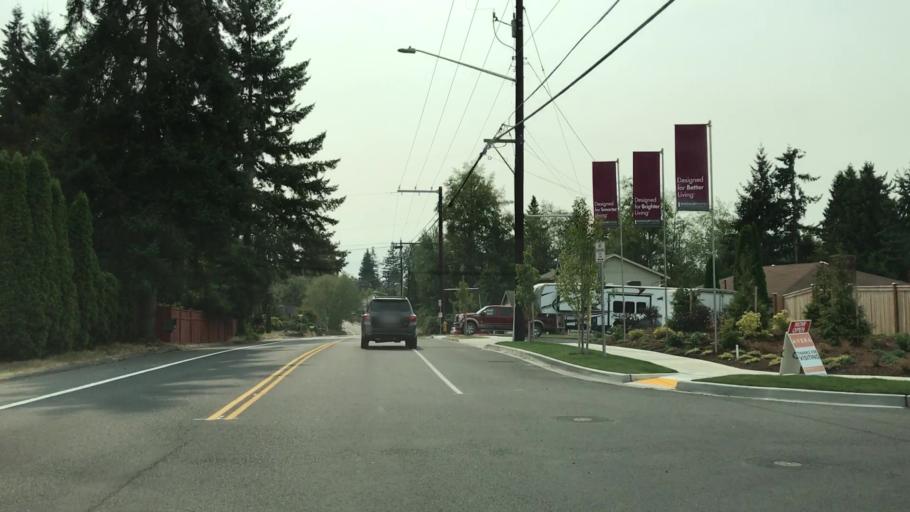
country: US
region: Washington
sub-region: Snohomish County
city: Martha Lake
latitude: 47.8581
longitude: -122.2478
